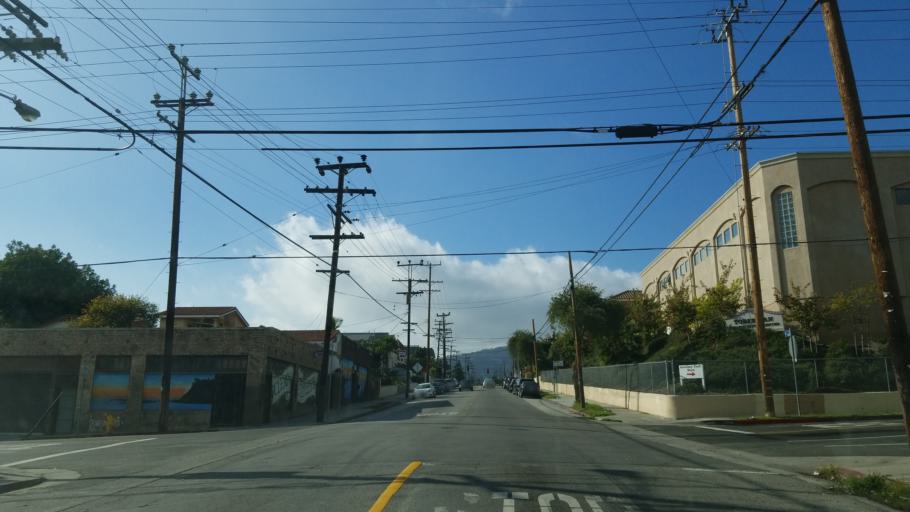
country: US
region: California
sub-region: Los Angeles County
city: San Pedro
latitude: 33.7433
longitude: -118.2899
